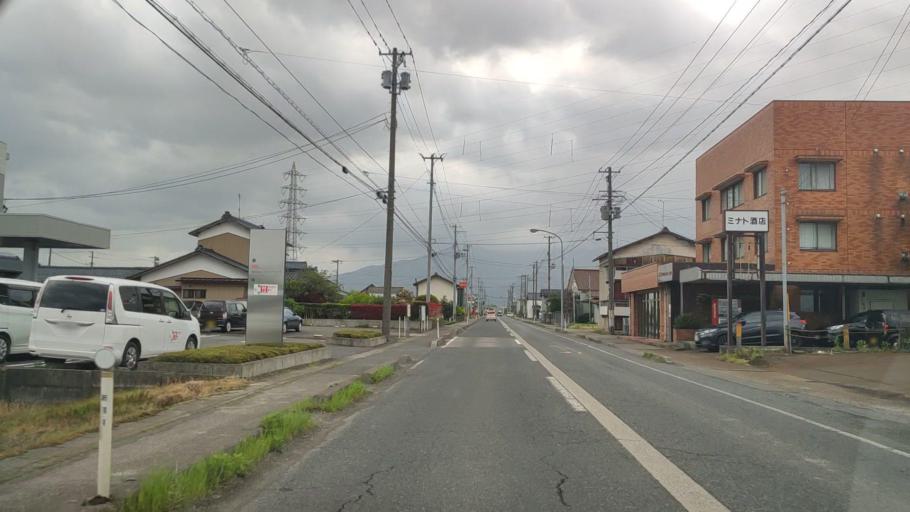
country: JP
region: Niigata
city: Gosen
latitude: 37.7344
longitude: 139.1953
